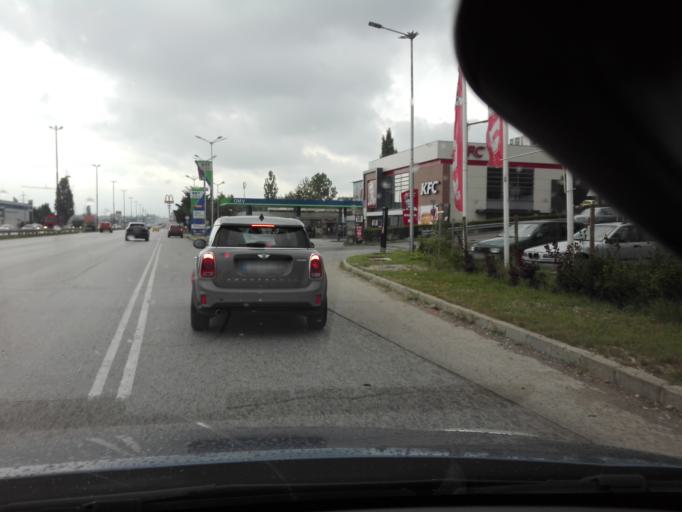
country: BG
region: Sofia-Capital
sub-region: Stolichna Obshtina
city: Sofia
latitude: 42.6521
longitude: 23.2866
